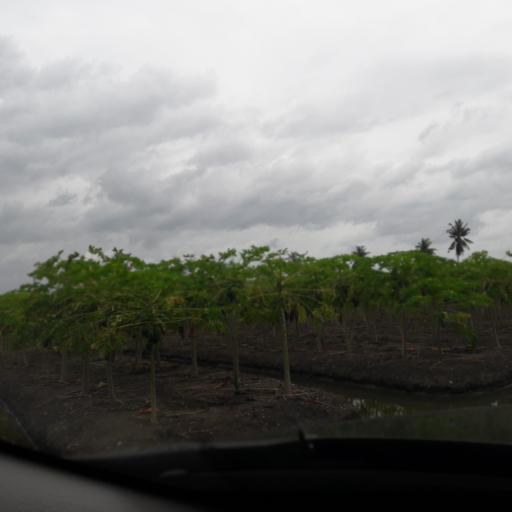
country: TH
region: Ratchaburi
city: Damnoen Saduak
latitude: 13.5743
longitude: 99.9411
